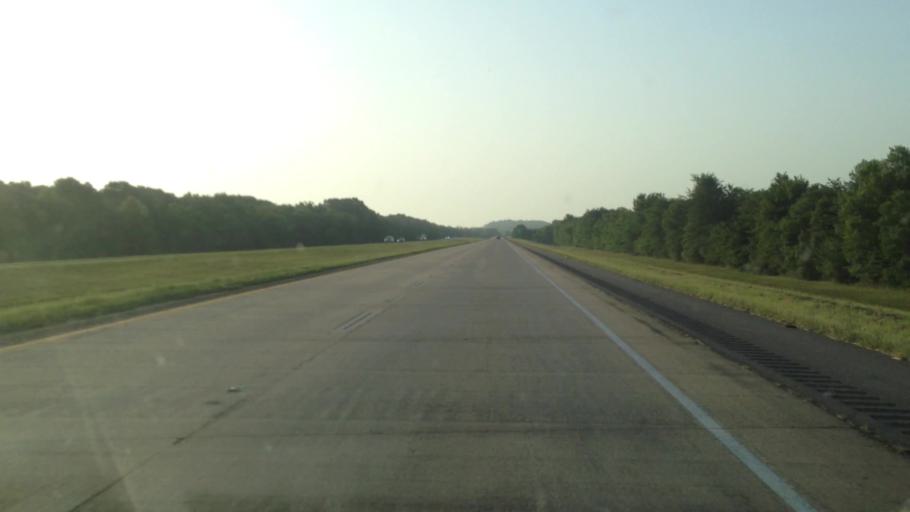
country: US
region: Louisiana
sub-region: Grant Parish
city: Colfax
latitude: 31.5049
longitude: -92.8817
